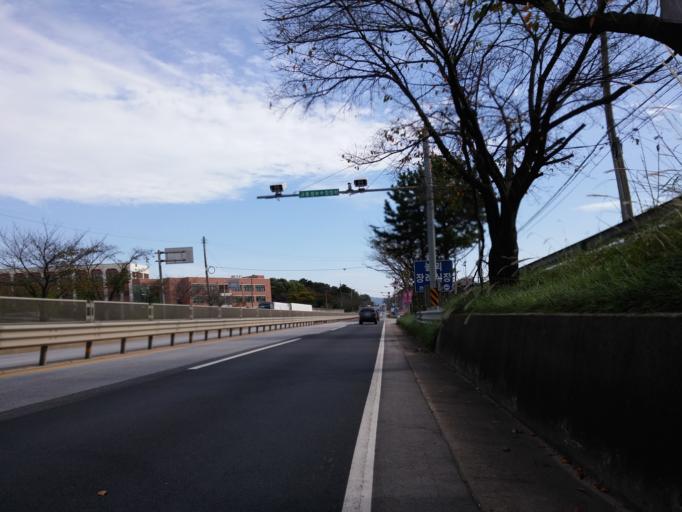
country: KR
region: Chungcheongnam-do
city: Nonsan
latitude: 36.1848
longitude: 127.0931
